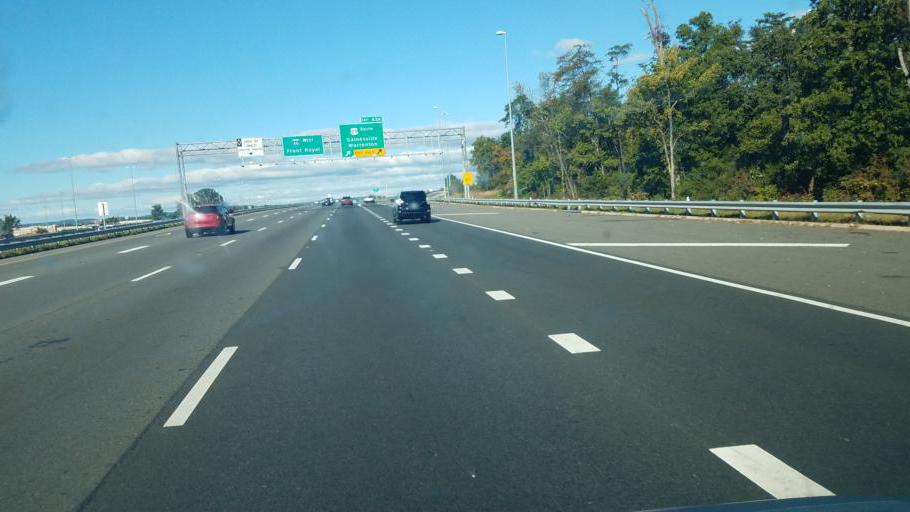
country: US
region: Virginia
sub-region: Prince William County
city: Gainesville
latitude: 38.7991
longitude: -77.5923
